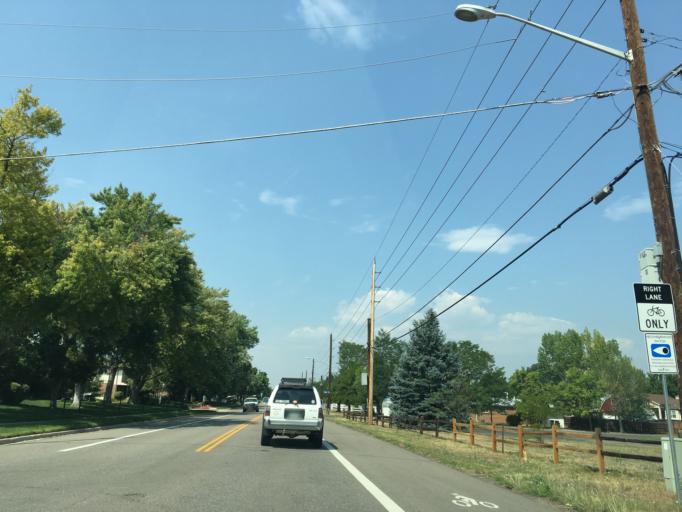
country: US
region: Colorado
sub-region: Jefferson County
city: Applewood
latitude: 39.7475
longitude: -105.1234
